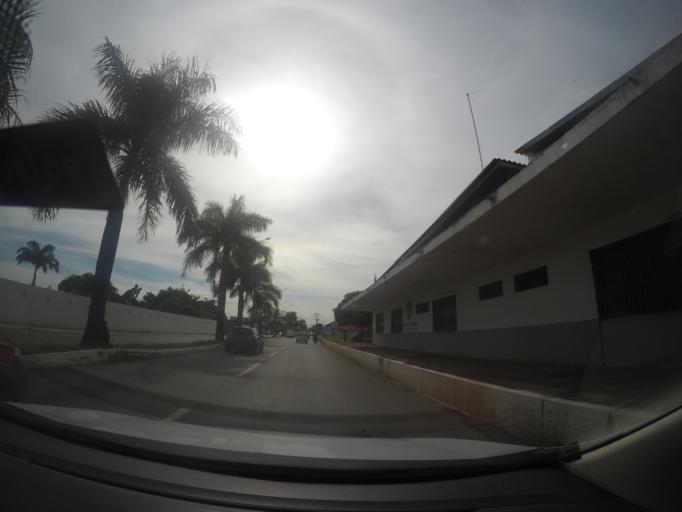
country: BR
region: Goias
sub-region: Goiania
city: Goiania
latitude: -16.6636
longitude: -49.2857
